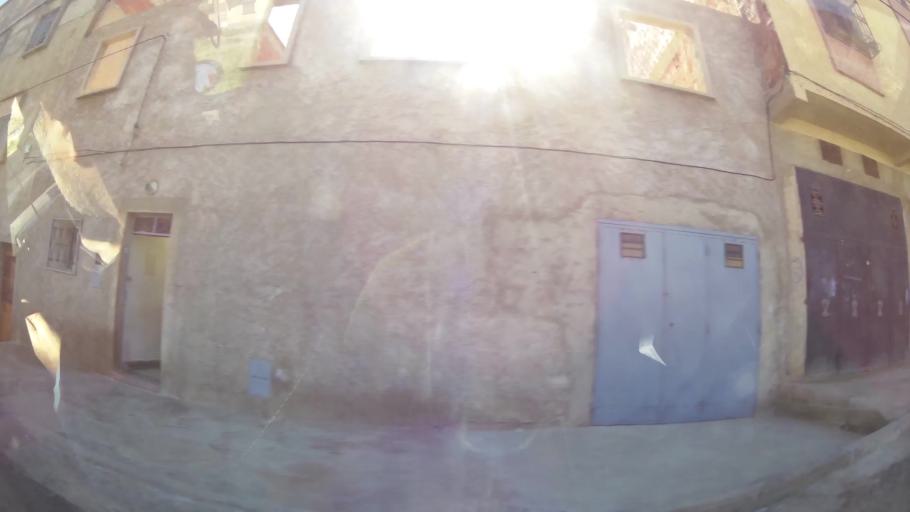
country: MA
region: Oriental
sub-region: Oujda-Angad
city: Oujda
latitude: 34.6560
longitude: -1.9369
